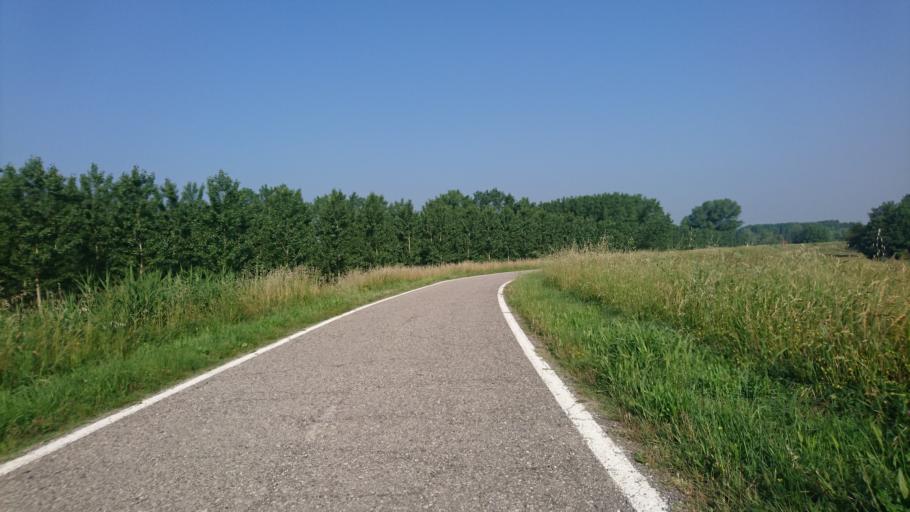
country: IT
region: Veneto
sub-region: Provincia di Rovigo
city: Castelnovo Bariano
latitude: 45.0219
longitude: 11.2760
